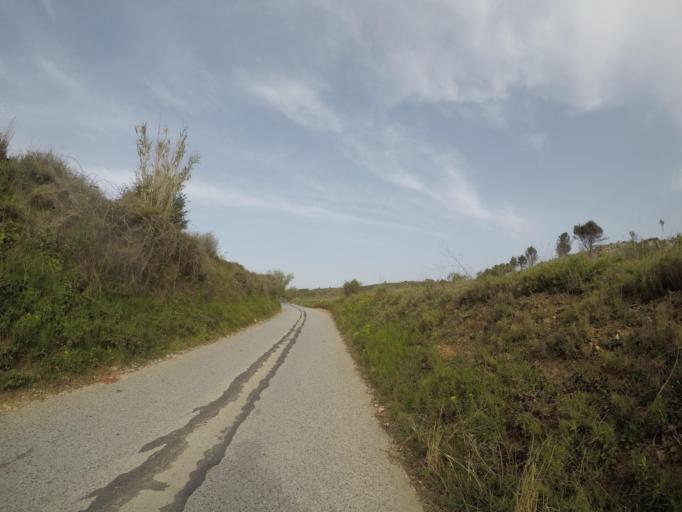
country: FR
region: Languedoc-Roussillon
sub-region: Departement des Pyrenees-Orientales
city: Baixas
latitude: 42.7679
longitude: 2.8104
